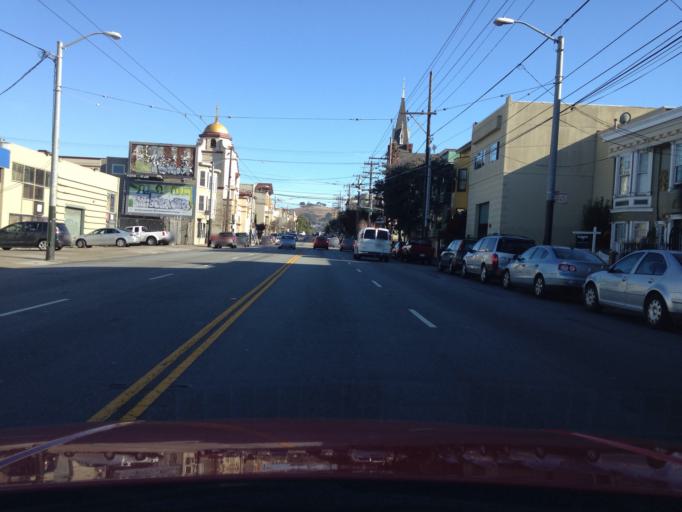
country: US
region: California
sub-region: San Francisco County
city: San Francisco
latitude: 37.7629
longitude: -122.4173
